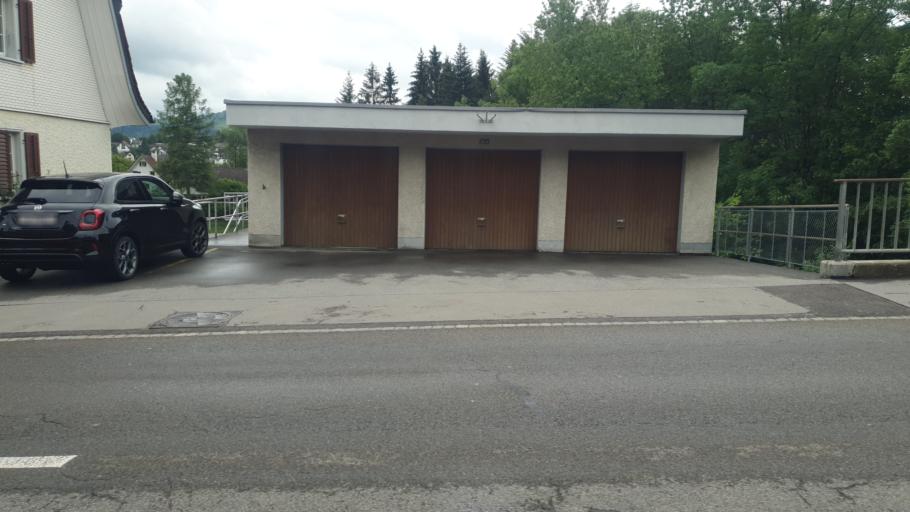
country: CH
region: Appenzell Ausserrhoden
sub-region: Bezirk Mittelland
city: Teufen
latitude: 47.3907
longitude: 9.3838
